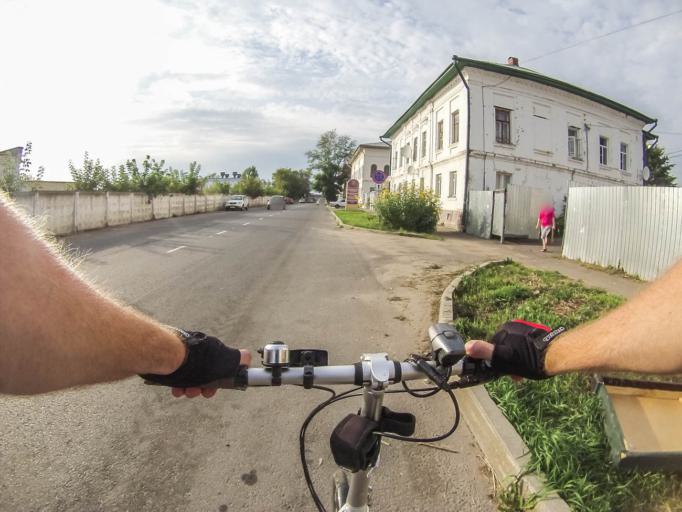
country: RU
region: Kostroma
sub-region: Kostromskoy Rayon
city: Kostroma
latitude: 57.7686
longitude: 40.9142
